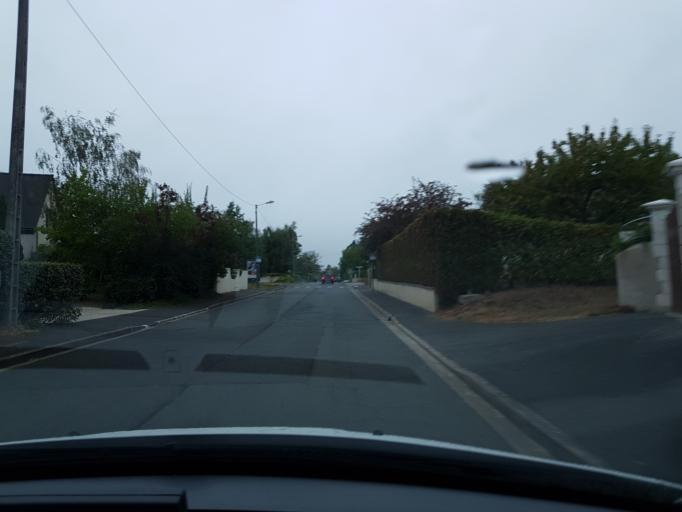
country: FR
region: Centre
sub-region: Departement d'Indre-et-Loire
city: Saint-Avertin
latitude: 47.3624
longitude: 0.7525
